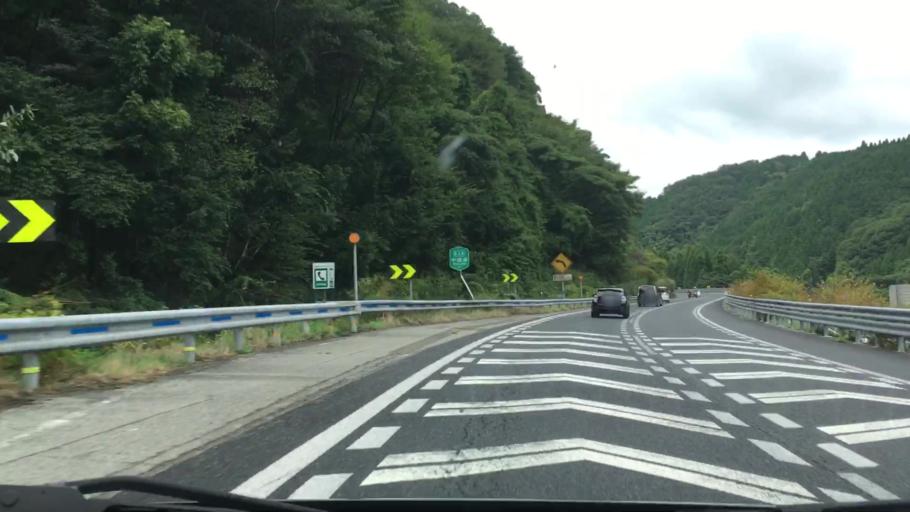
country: JP
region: Okayama
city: Tsuyama
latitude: 35.0147
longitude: 134.2422
